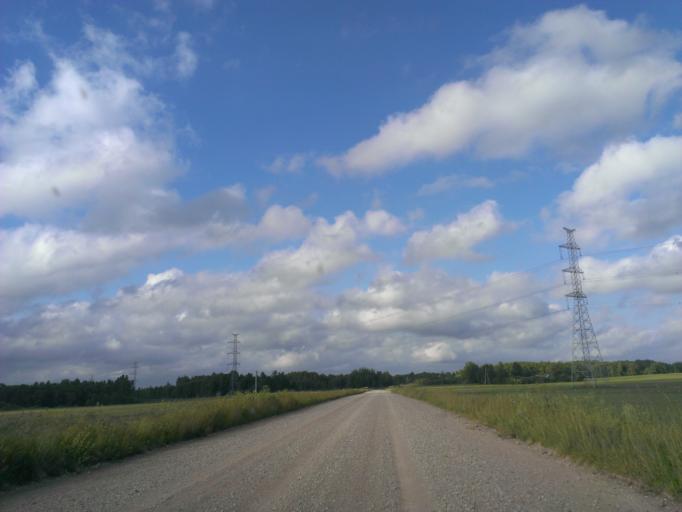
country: LV
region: Aizpute
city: Aizpute
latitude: 56.7823
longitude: 21.4843
